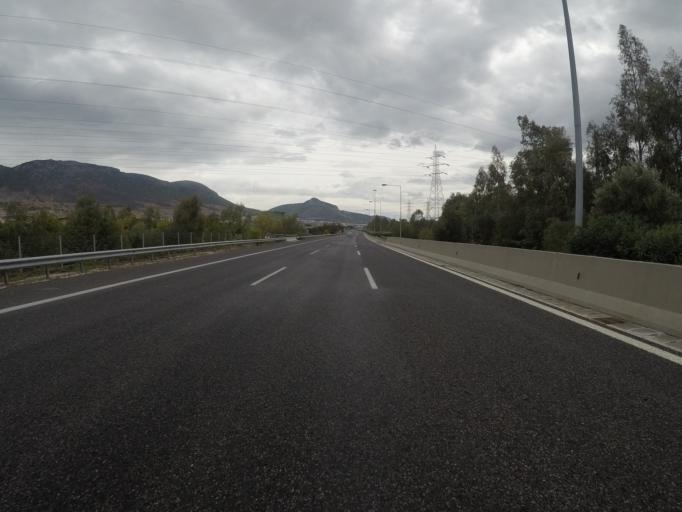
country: GR
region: Attica
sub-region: Nomarchia Dytikis Attikis
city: Aspropyrgos
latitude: 38.0947
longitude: 23.5761
